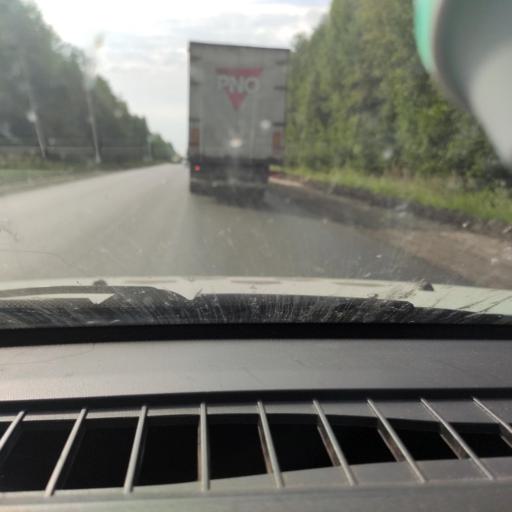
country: RU
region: Kirov
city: Chernaya Kholunitsa
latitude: 58.8790
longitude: 51.4539
